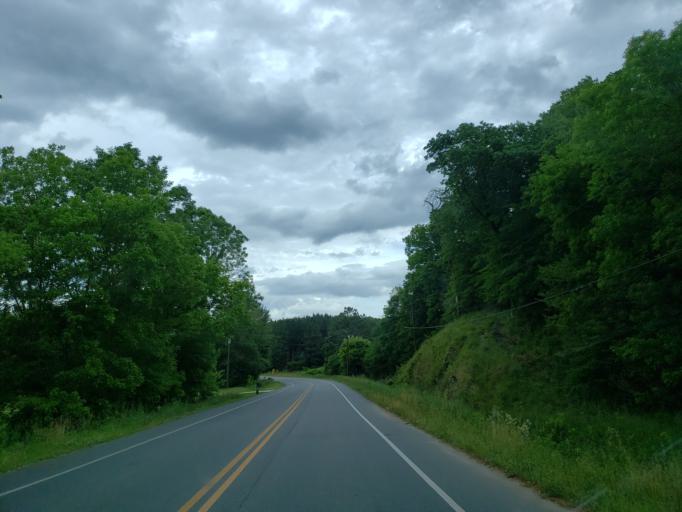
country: US
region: Georgia
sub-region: Polk County
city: Rockmart
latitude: 33.9795
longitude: -85.0431
